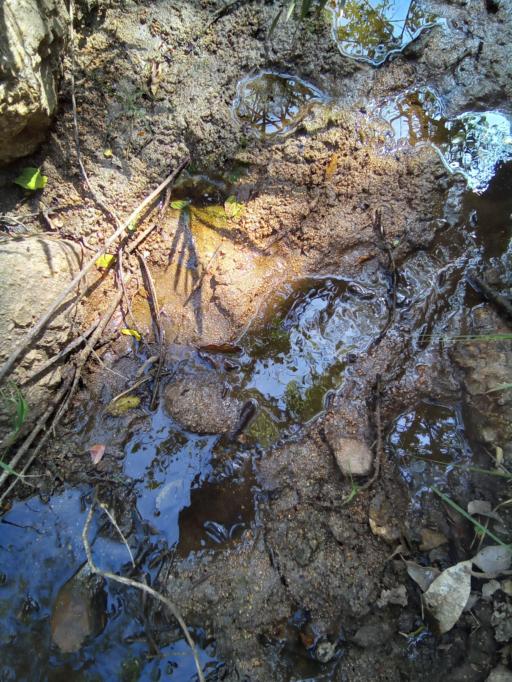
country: KE
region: Homa Bay
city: Homa Bay
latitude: -0.4901
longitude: 34.1875
